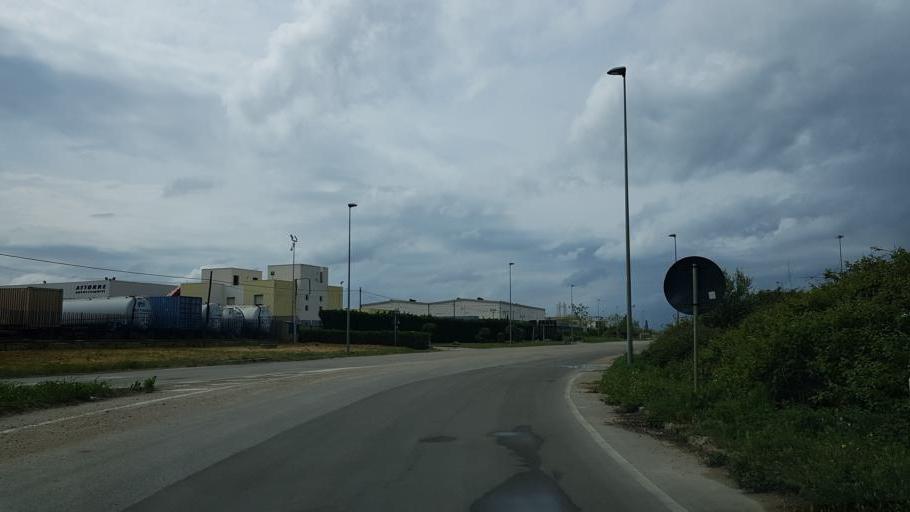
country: IT
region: Apulia
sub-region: Provincia di Brindisi
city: Materdomini
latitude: 40.6381
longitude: 17.9757
